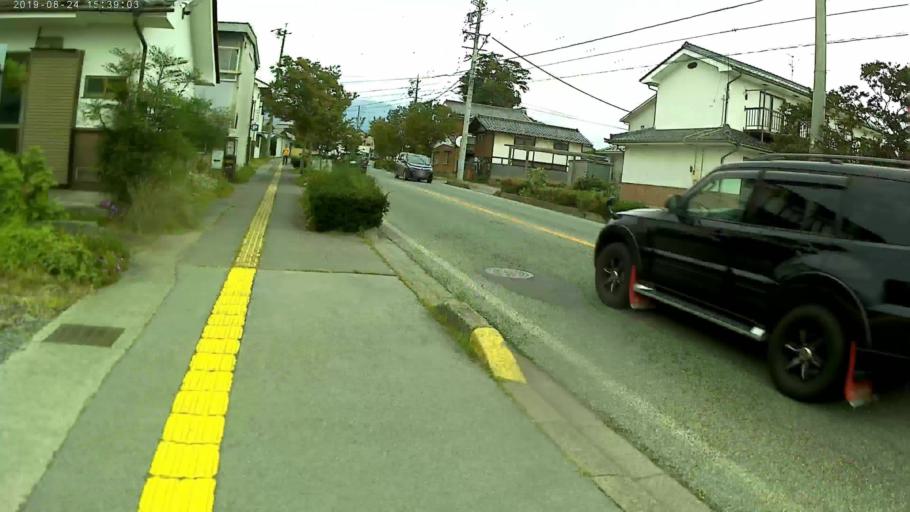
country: JP
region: Nagano
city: Komoro
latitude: 36.2780
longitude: 138.4783
